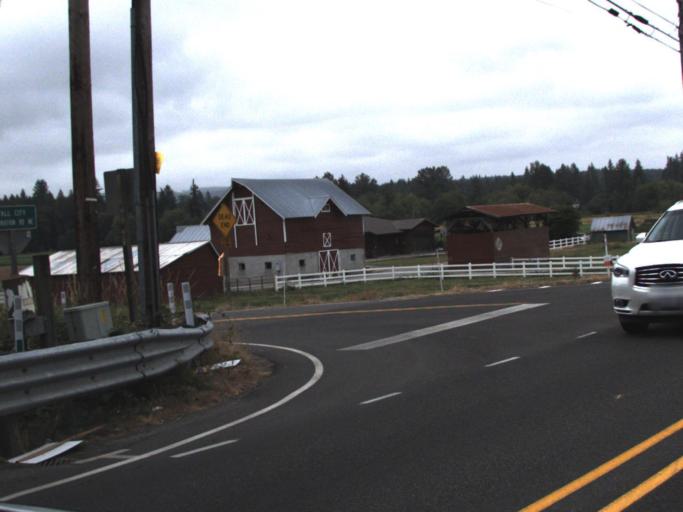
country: US
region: Washington
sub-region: King County
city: Carnation
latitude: 47.6372
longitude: -121.9163
